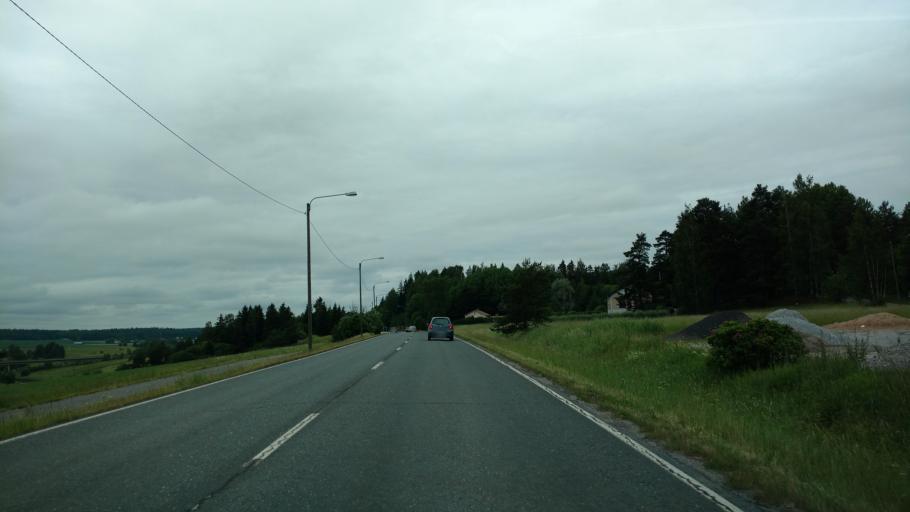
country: FI
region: Varsinais-Suomi
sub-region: Salo
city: Halikko
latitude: 60.4068
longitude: 23.0656
